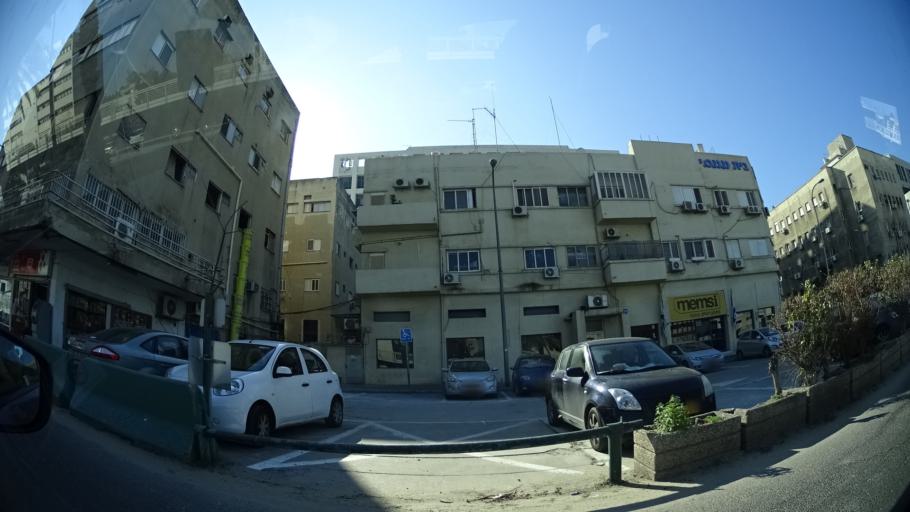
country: IL
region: Tel Aviv
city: Tel Aviv
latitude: 32.0634
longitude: 34.7781
